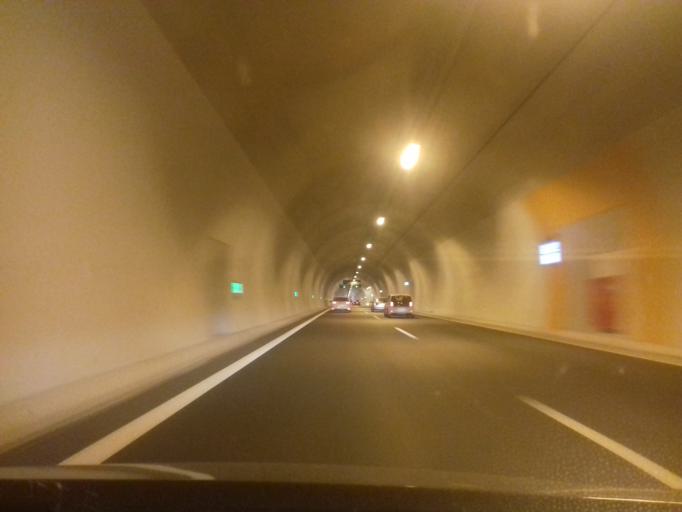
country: GR
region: West Greece
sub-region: Nomos Achaias
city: Aiyira
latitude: 38.1385
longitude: 22.3798
